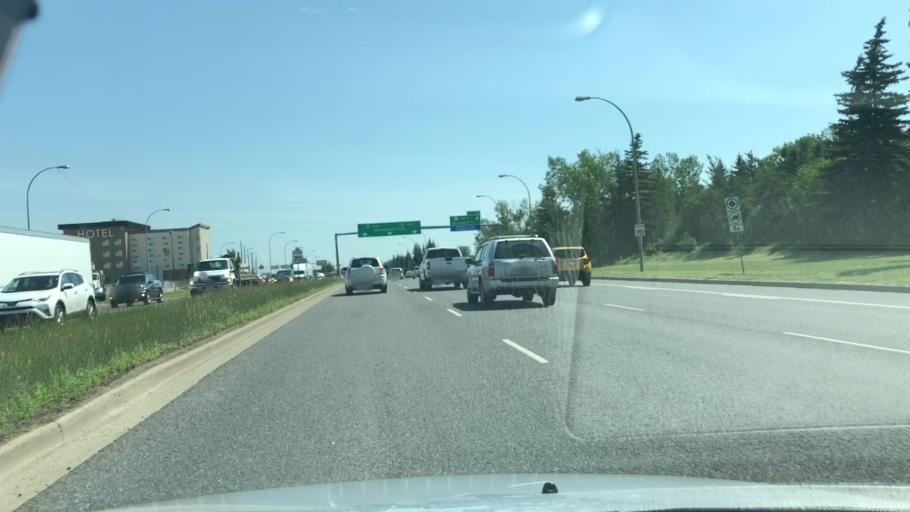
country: CA
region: Alberta
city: St. Albert
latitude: 53.5811
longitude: -113.5641
